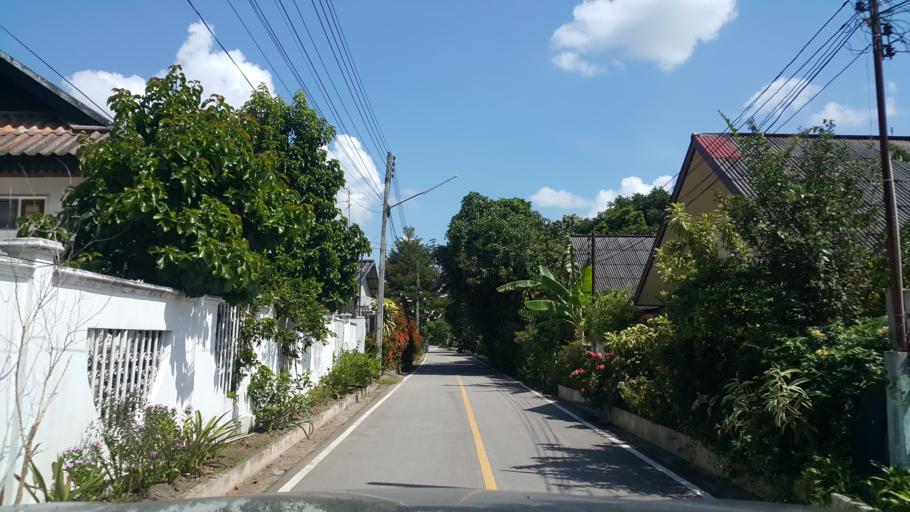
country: TH
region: Chiang Mai
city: Chom Thong
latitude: 18.4206
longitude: 98.6809
